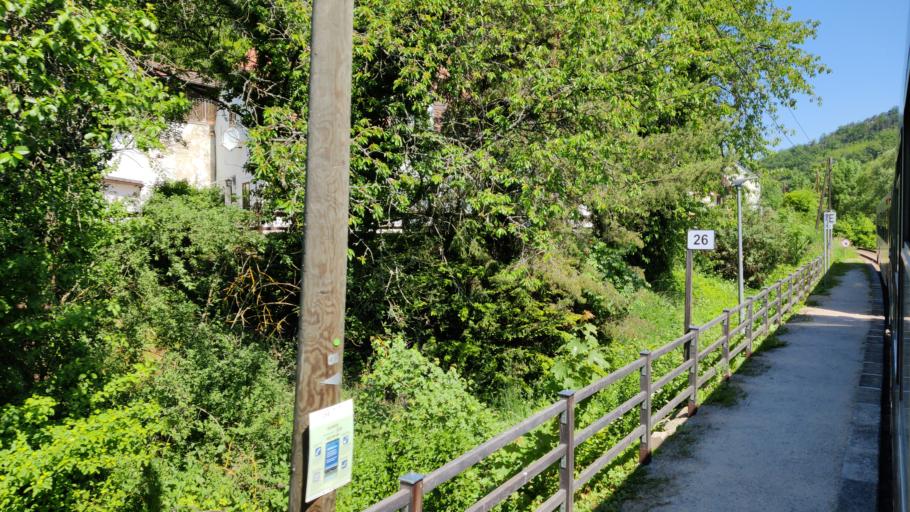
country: AT
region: Lower Austria
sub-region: Politischer Bezirk Horn
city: Gars am Kamp
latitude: 48.5759
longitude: 15.6587
